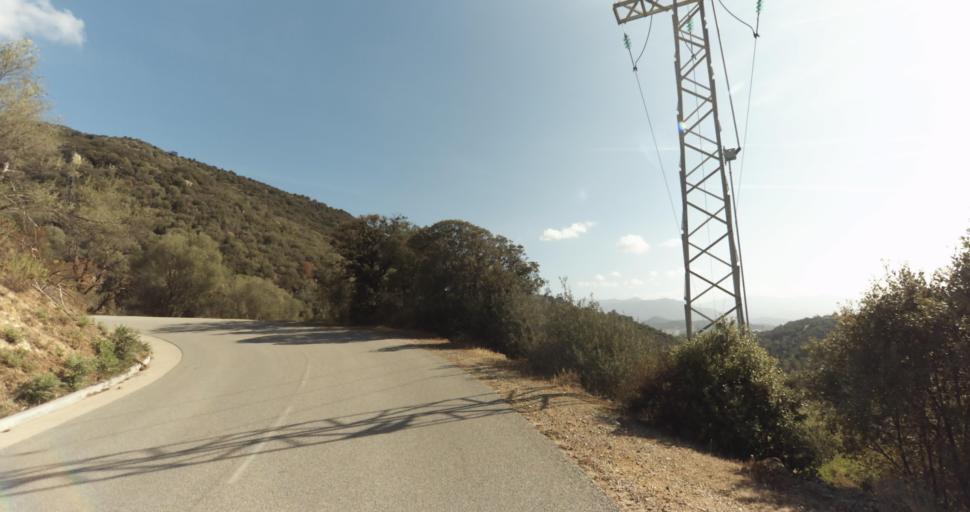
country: FR
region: Corsica
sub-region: Departement de la Corse-du-Sud
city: Ajaccio
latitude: 41.9310
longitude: 8.7040
